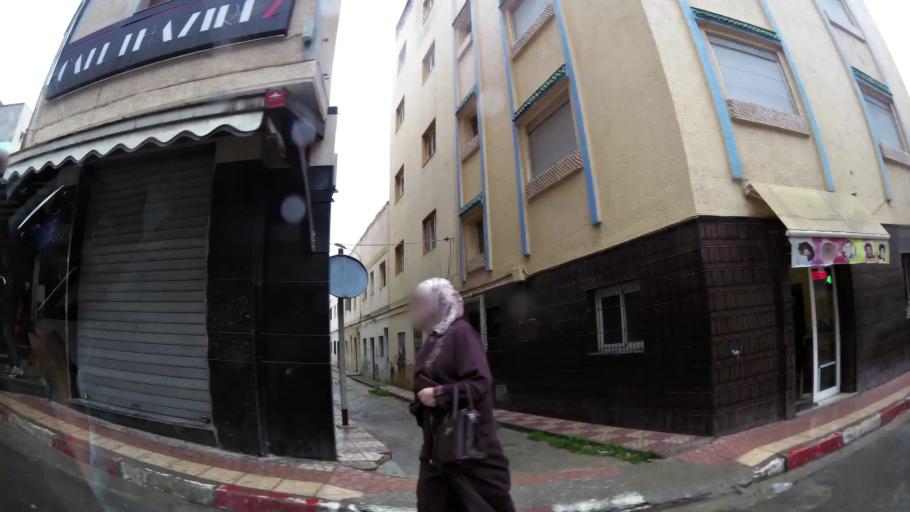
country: MA
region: Taza-Al Hoceima-Taounate
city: Al Hoceima
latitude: 35.2507
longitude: -3.9347
